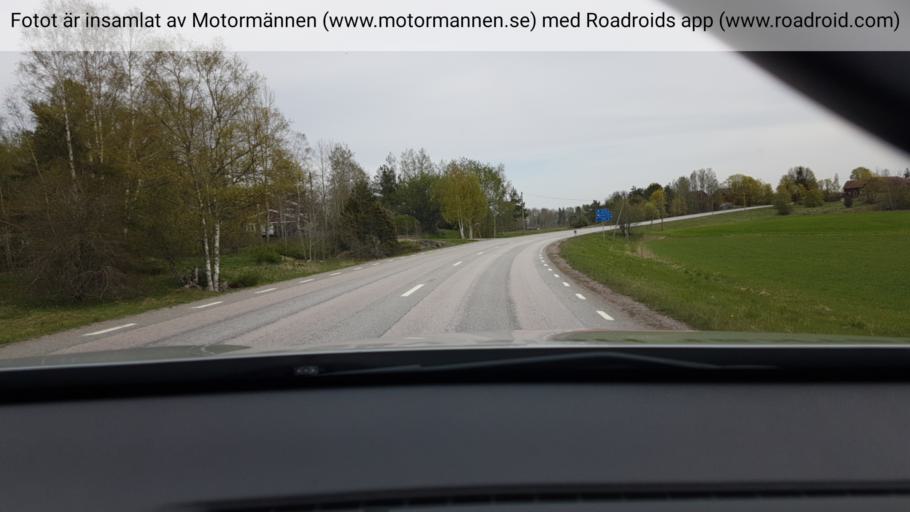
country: SE
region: Uppsala
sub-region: Osthammars Kommun
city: Gimo
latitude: 59.9556
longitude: 18.1145
